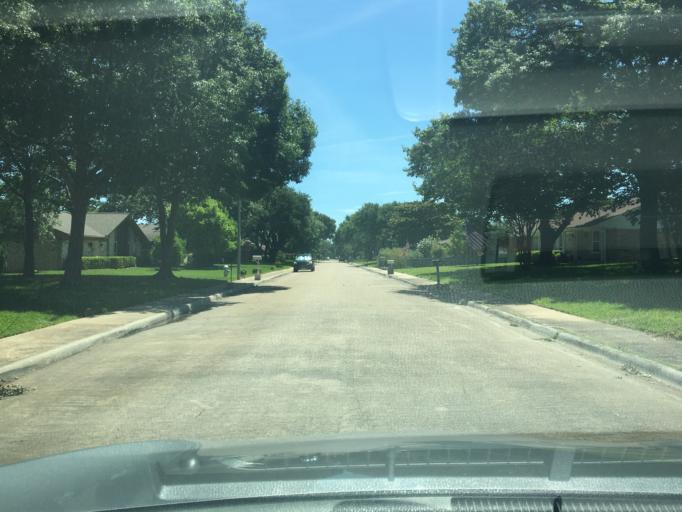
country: US
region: Texas
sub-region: Dallas County
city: Richardson
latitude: 32.9476
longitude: -96.6940
